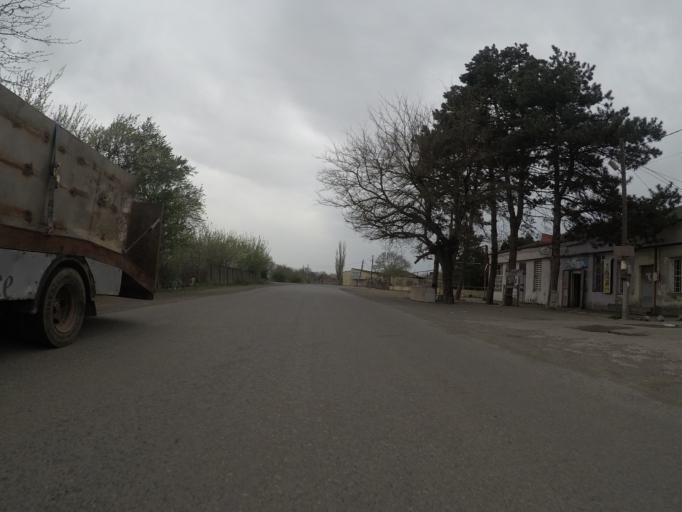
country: GE
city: Agara
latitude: 42.0211
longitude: 43.7293
